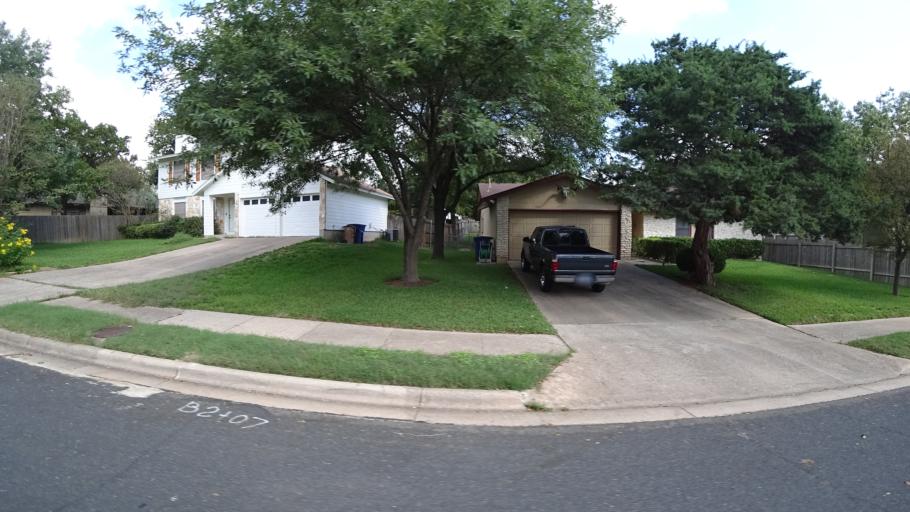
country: US
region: Texas
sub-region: Travis County
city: Shady Hollow
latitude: 30.1977
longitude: -97.8123
